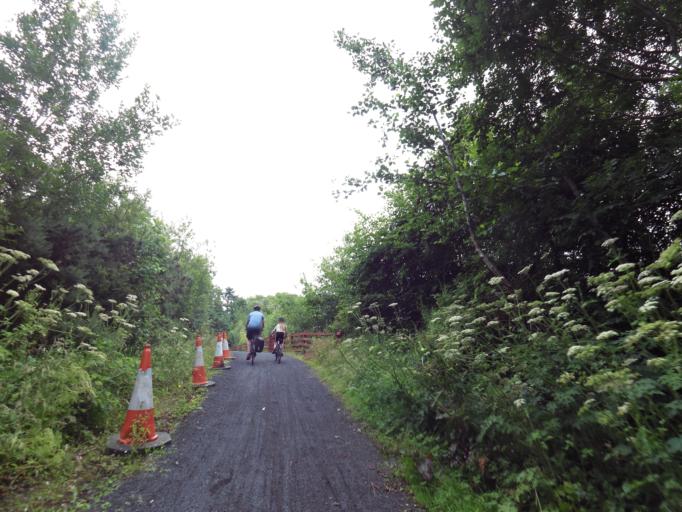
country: IE
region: Connaught
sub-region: Maigh Eo
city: Westport
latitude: 53.8155
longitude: -9.5372
